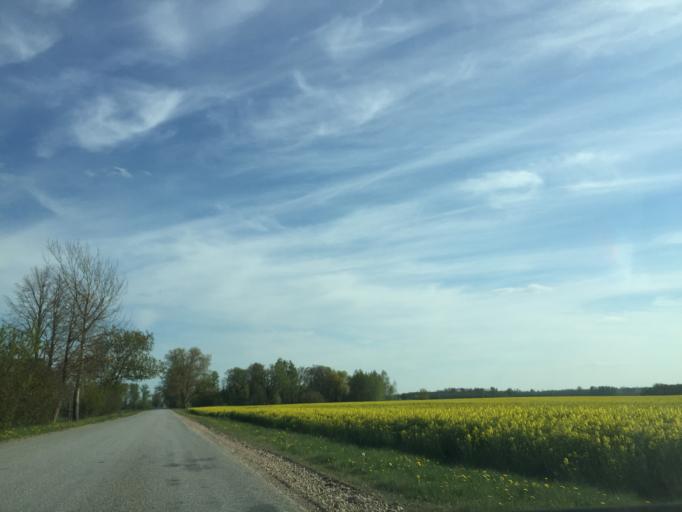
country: LV
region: Bauskas Rajons
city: Bauska
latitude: 56.3594
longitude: 24.2313
